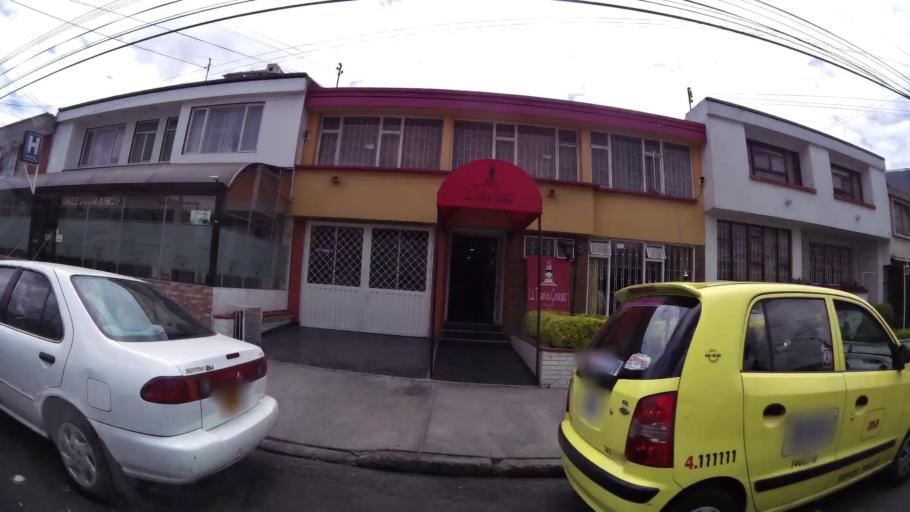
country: CO
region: Bogota D.C.
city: Bogota
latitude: 4.6333
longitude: -74.0938
